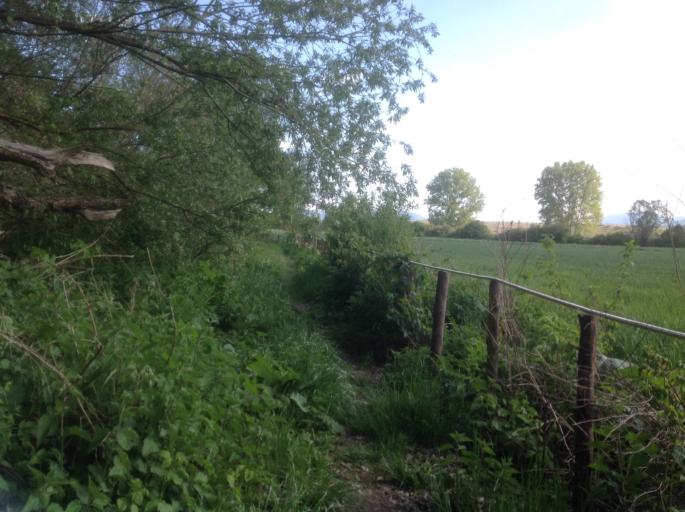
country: IT
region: Latium
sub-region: Provincia di Rieti
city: Colli sul Velino
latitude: 42.4699
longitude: 12.8055
